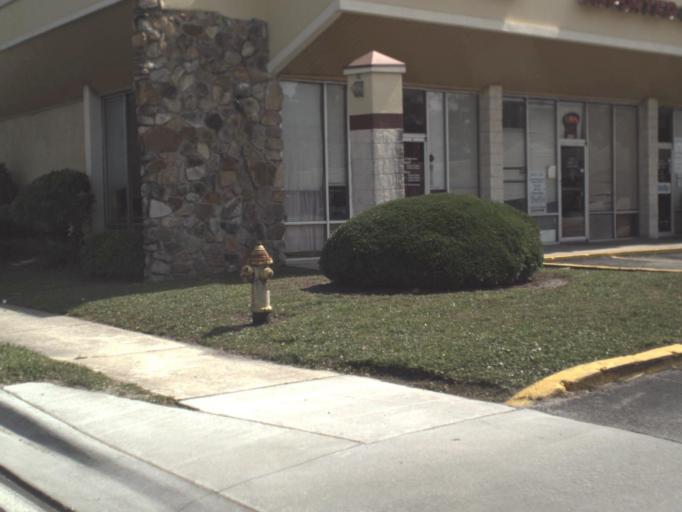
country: US
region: Florida
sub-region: Duval County
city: Jacksonville
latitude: 30.2788
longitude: -81.6027
